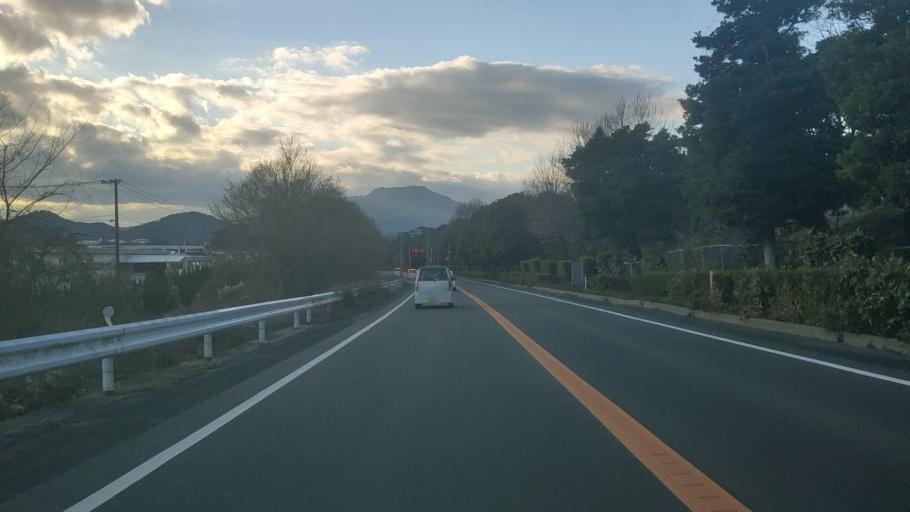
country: JP
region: Saga Prefecture
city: Takeocho-takeo
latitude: 33.2881
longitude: 130.1400
